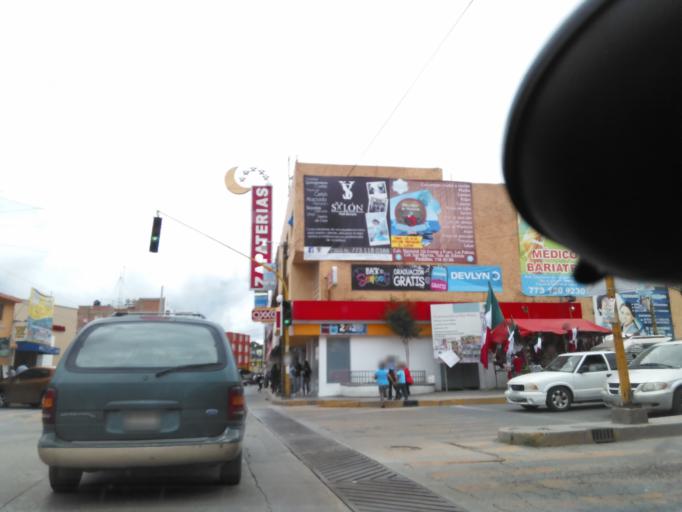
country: MX
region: Hidalgo
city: Tula de Allende
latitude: 20.0557
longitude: -99.3402
